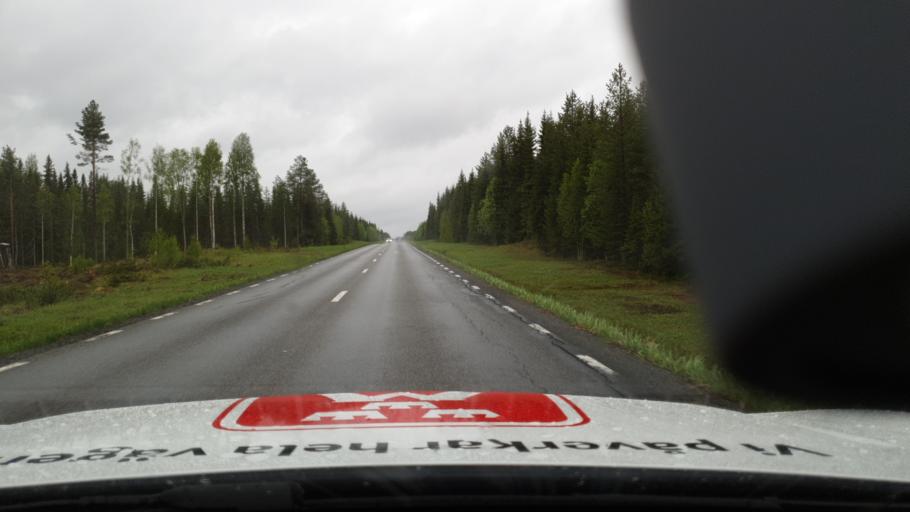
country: SE
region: Jaemtland
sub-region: Stroemsunds Kommun
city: Stroemsund
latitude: 63.7218
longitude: 15.4744
